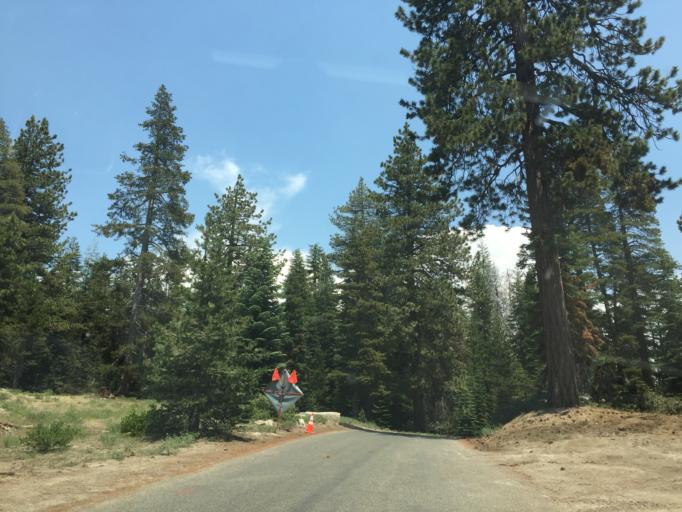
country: US
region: California
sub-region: Tulare County
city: Three Rivers
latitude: 36.7096
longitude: -118.8735
